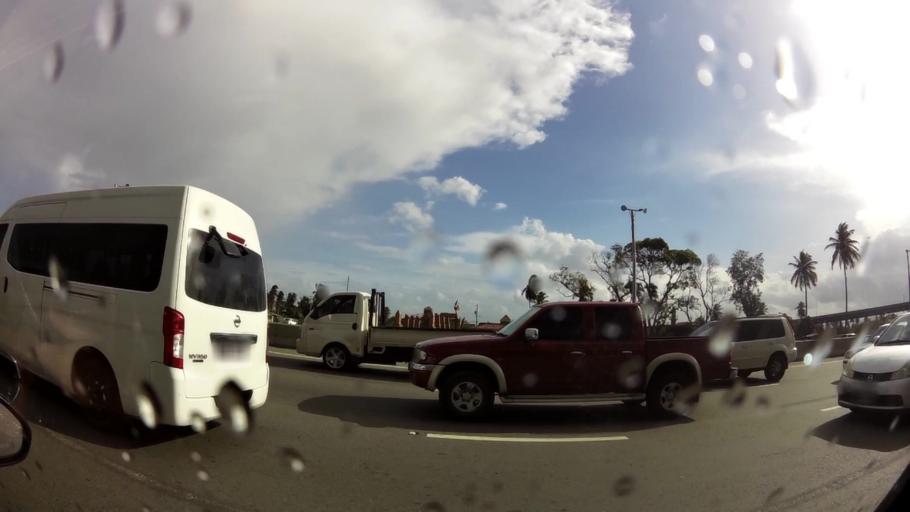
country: TT
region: Tunapuna/Piarco
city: Tunapuna
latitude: 10.6333
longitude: -61.4274
